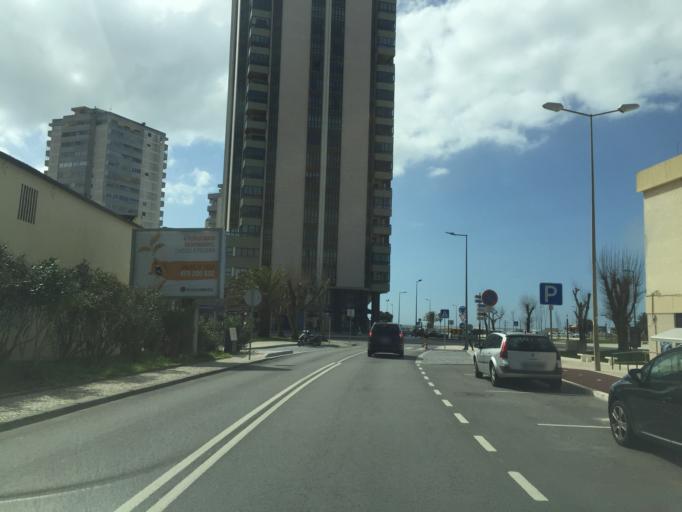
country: PT
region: Coimbra
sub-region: Figueira da Foz
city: Buarcos
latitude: 40.1644
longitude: -8.8719
